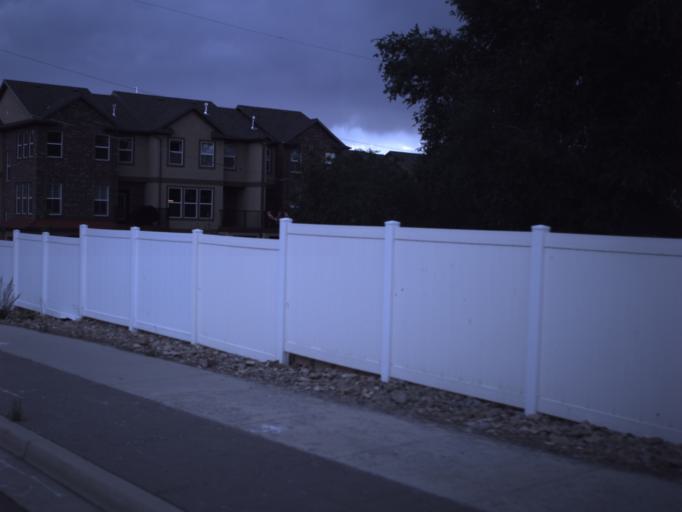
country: US
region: Utah
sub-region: Salt Lake County
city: Draper
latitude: 40.5347
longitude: -111.8712
